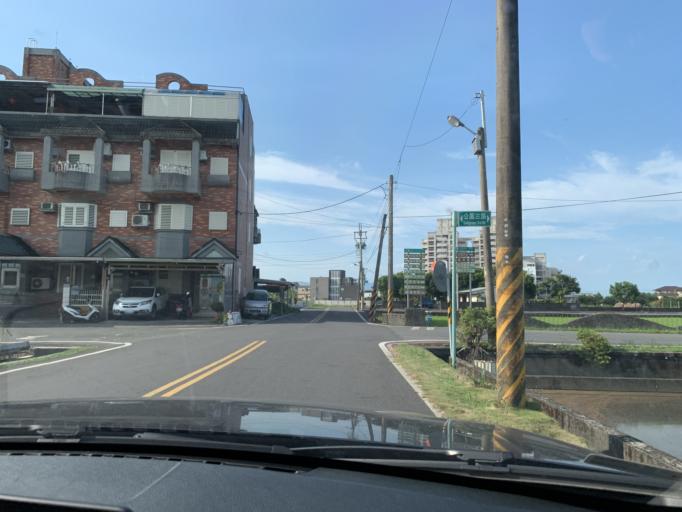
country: TW
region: Taiwan
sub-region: Yilan
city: Yilan
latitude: 24.6780
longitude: 121.8099
